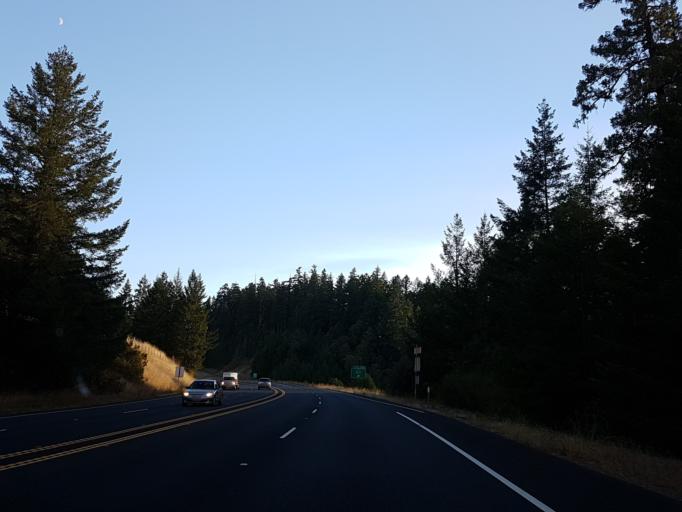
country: US
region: California
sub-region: Humboldt County
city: Redway
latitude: 39.9504
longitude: -123.7812
